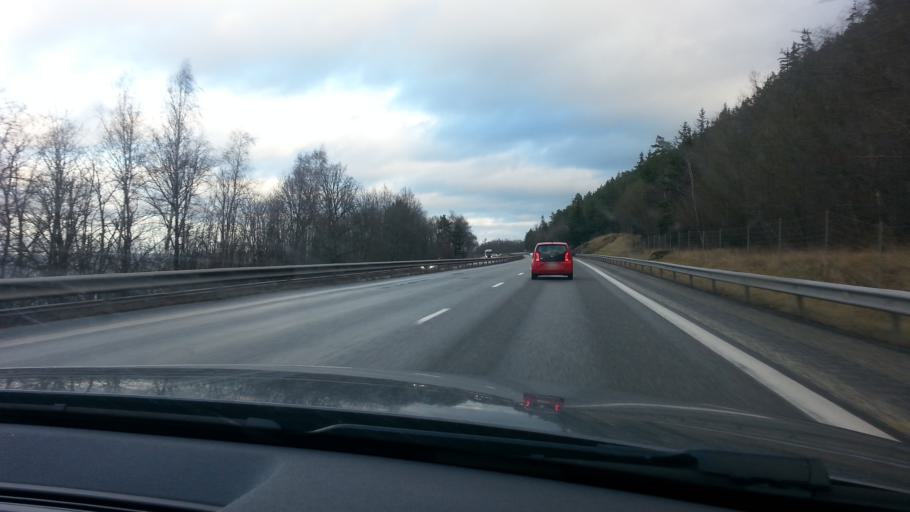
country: SE
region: Joenkoeping
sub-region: Jonkopings Kommun
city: Kaxholmen
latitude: 57.8826
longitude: 14.2809
